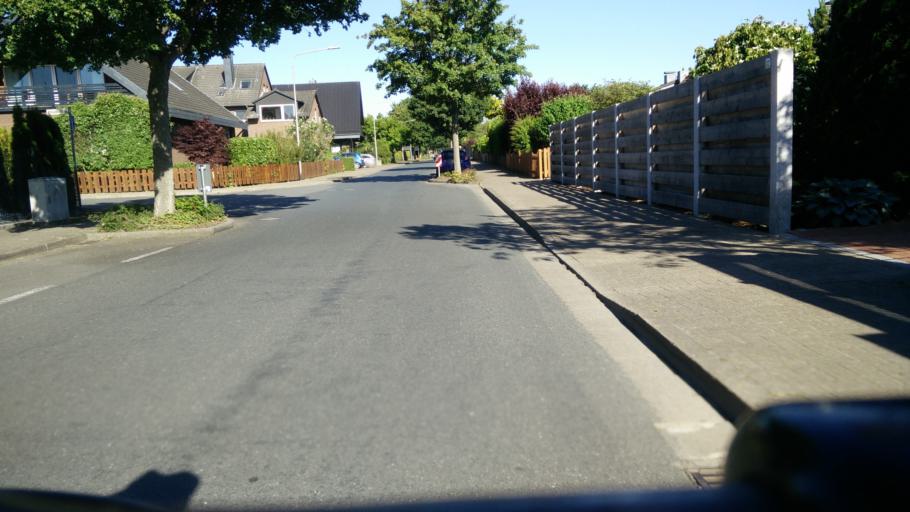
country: DE
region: Lower Saxony
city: Wunstorf
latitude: 52.4230
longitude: 9.4702
